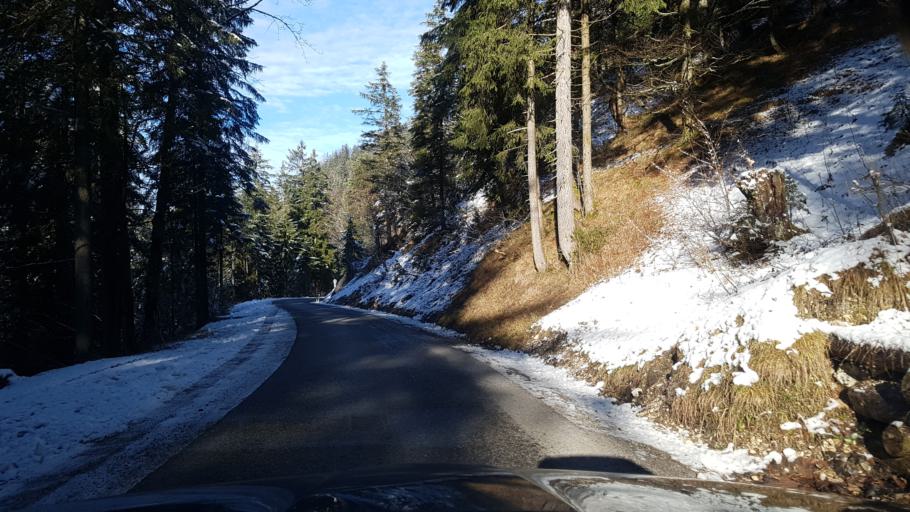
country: AT
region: Salzburg
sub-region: Politischer Bezirk Salzburg-Umgebung
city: Faistenau
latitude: 47.7639
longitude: 13.2285
